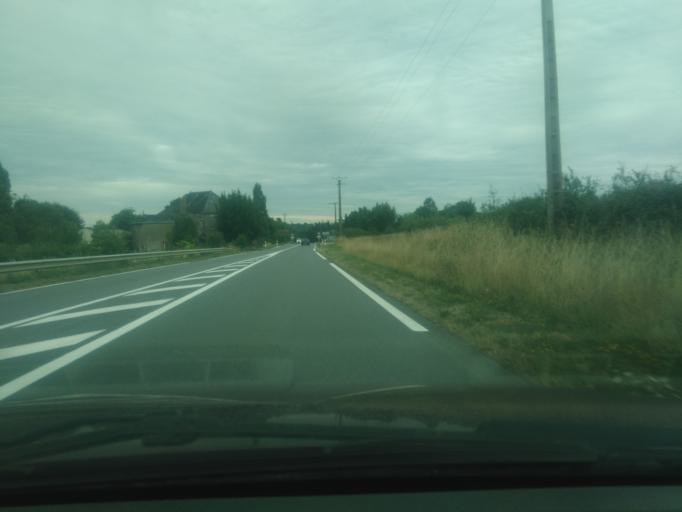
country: FR
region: Centre
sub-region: Departement de l'Indre
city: Neuvy-Saint-Sepulchre
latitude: 46.5737
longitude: 1.8859
